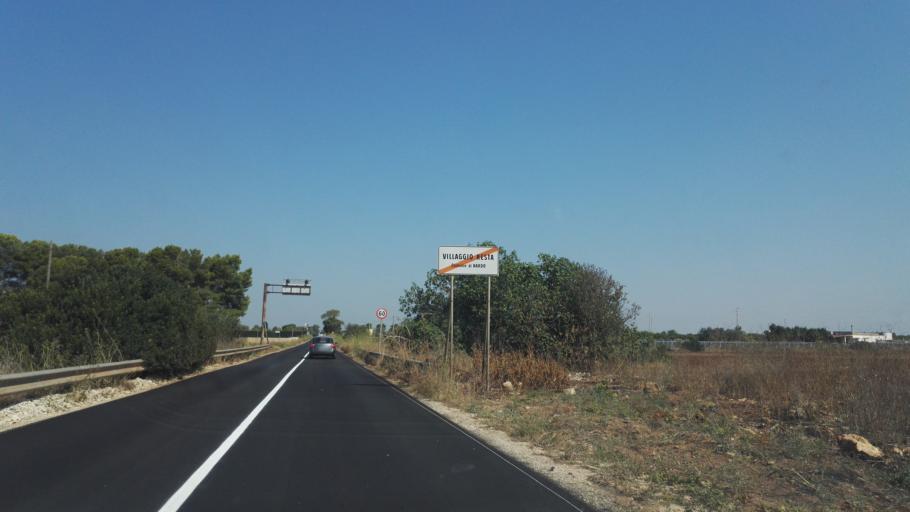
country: IT
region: Apulia
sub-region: Provincia di Lecce
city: Nardo
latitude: 40.2046
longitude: 17.9556
